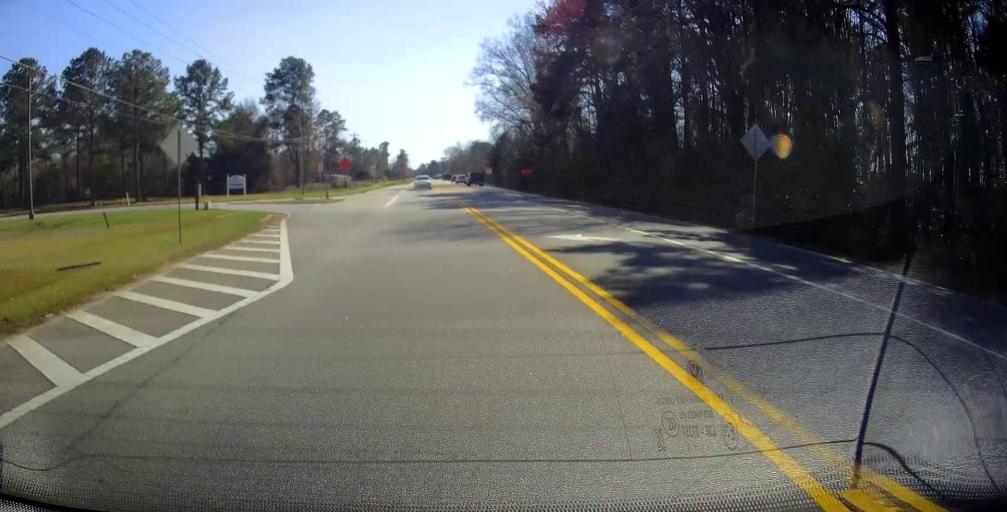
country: US
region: Georgia
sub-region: Houston County
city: Perry
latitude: 32.4850
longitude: -83.7300
